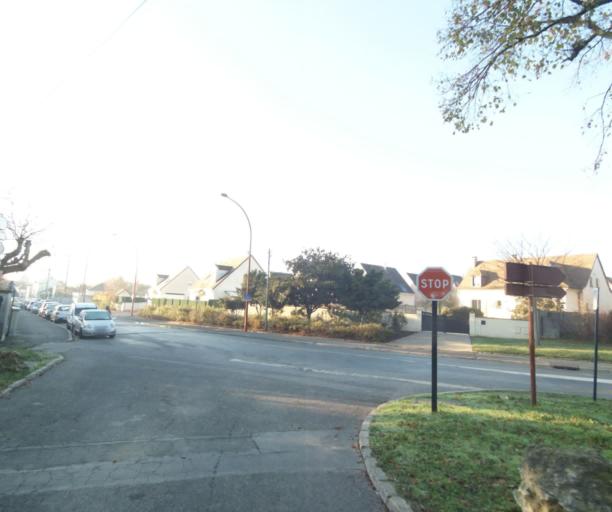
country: FR
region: Ile-de-France
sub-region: Departement du Val-d'Oise
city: Gonesse
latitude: 48.9906
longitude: 2.4464
